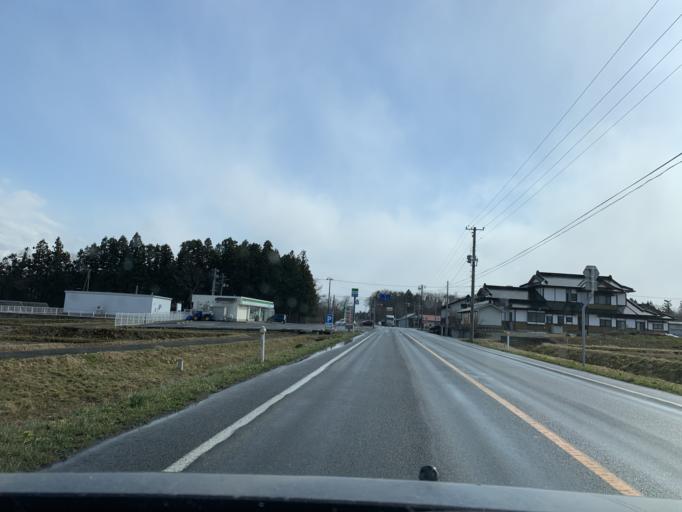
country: JP
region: Iwate
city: Kitakami
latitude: 39.2356
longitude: 141.0561
